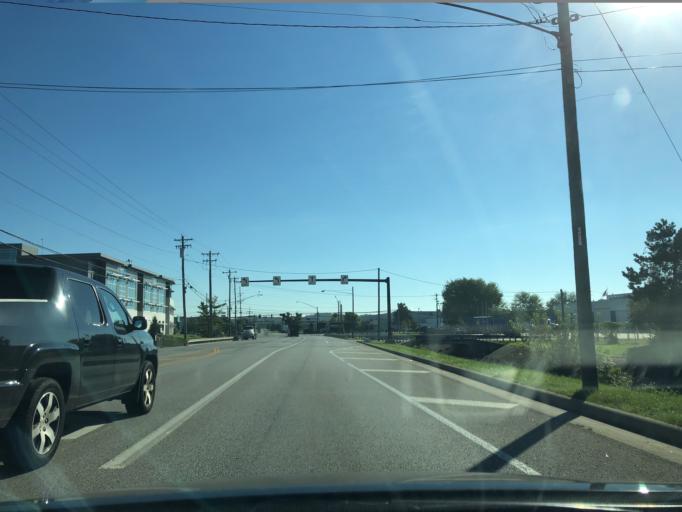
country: US
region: Ohio
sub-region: Hamilton County
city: Sharonville
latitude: 39.2844
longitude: -84.4320
